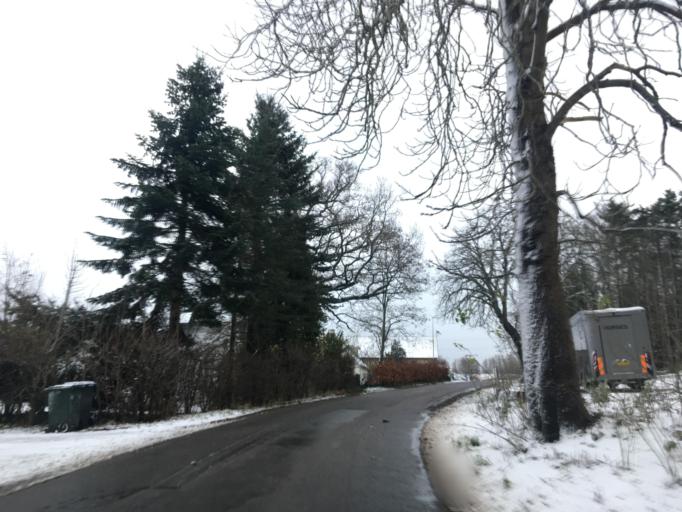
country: DK
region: Zealand
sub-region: Odsherred Kommune
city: Asnaes
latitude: 55.8305
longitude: 11.5695
